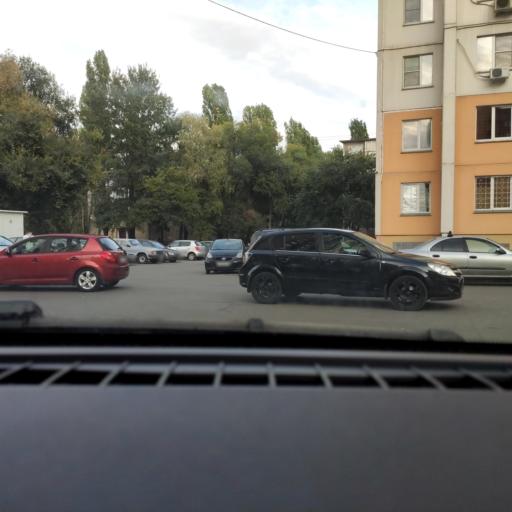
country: RU
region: Voronezj
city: Voronezh
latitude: 51.6491
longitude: 39.2353
